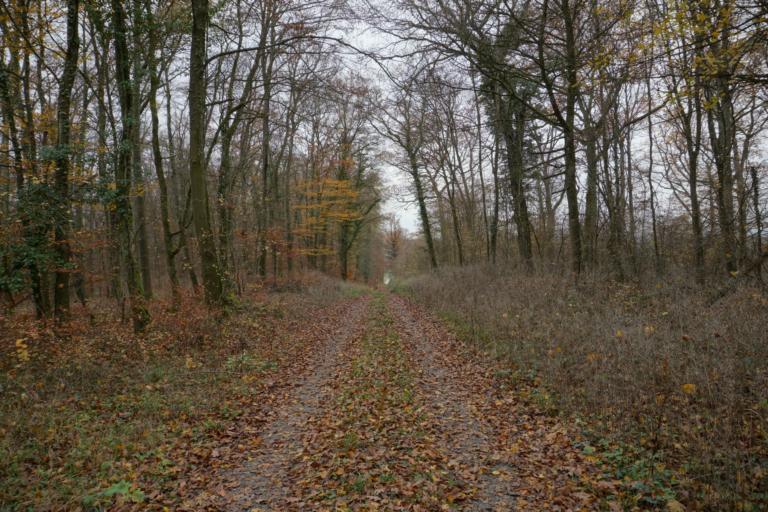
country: DE
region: Baden-Wuerttemberg
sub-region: Karlsruhe Region
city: Huffenhardt
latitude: 49.3044
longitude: 9.0384
